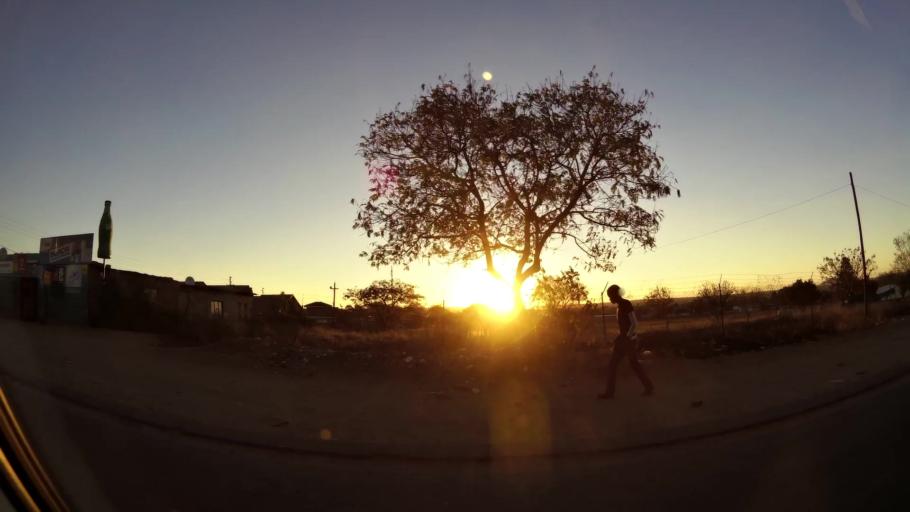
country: ZA
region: Limpopo
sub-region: Capricorn District Municipality
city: Polokwane
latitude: -23.8587
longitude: 29.3723
